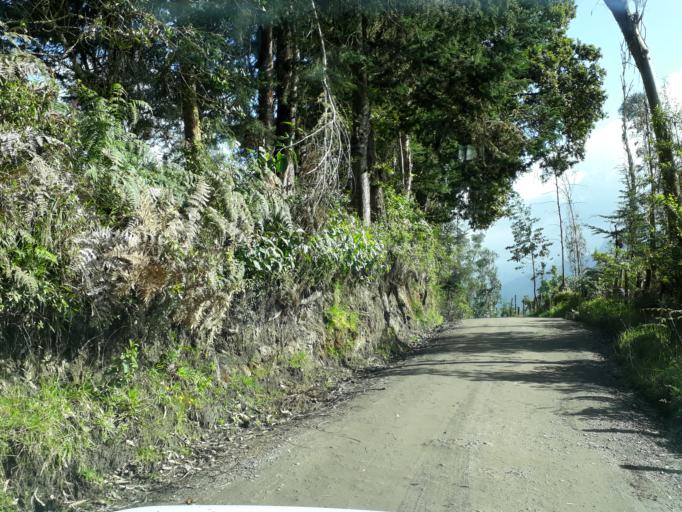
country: CO
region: Cundinamarca
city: Junin
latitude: 4.7899
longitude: -73.6782
